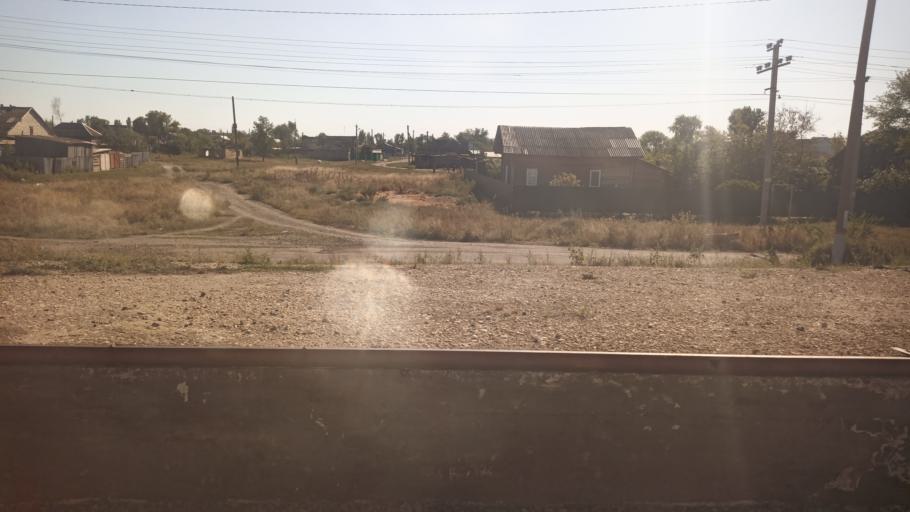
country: RU
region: Saratov
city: Pushkino
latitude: 51.2356
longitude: 46.9802
